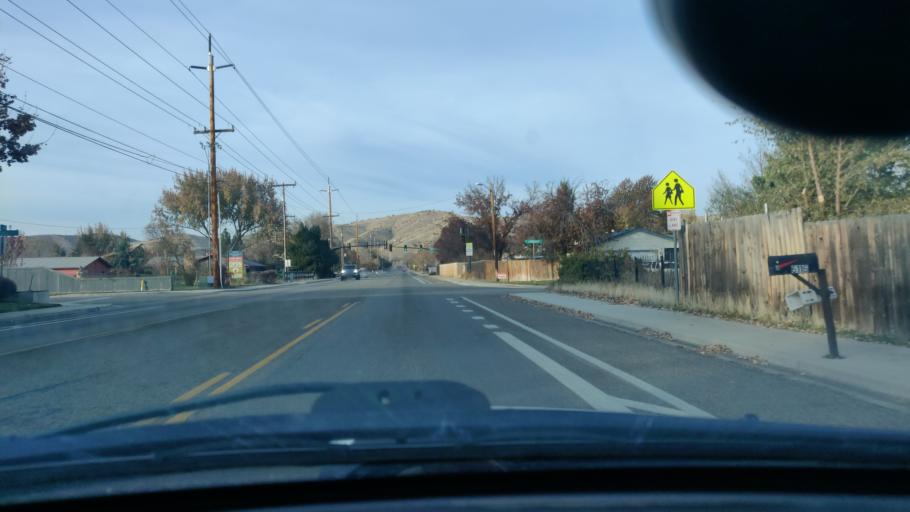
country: US
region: Idaho
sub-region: Ada County
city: Garden City
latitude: 43.6766
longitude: -116.2792
